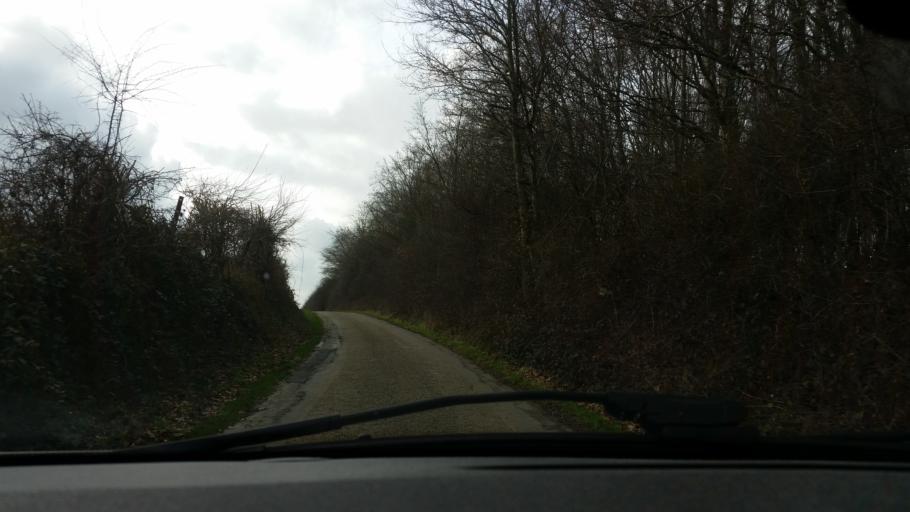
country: FR
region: Nord-Pas-de-Calais
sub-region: Departement du Nord
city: Jeumont
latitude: 50.2397
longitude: 4.1302
